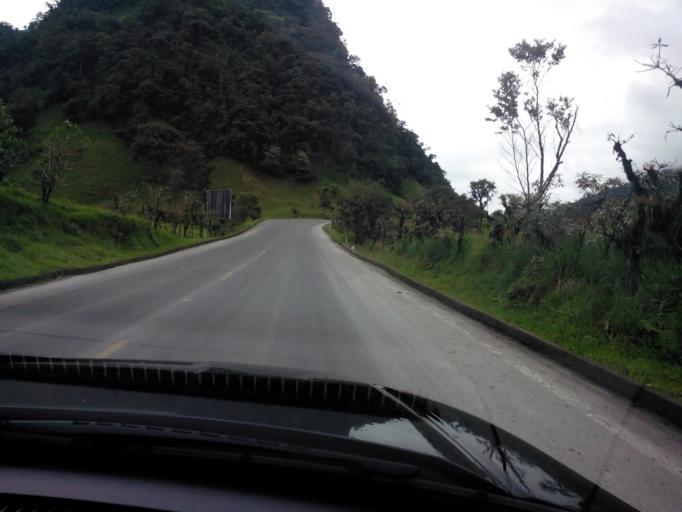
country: EC
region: Napo
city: Archidona
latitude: -0.5023
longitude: -77.8767
